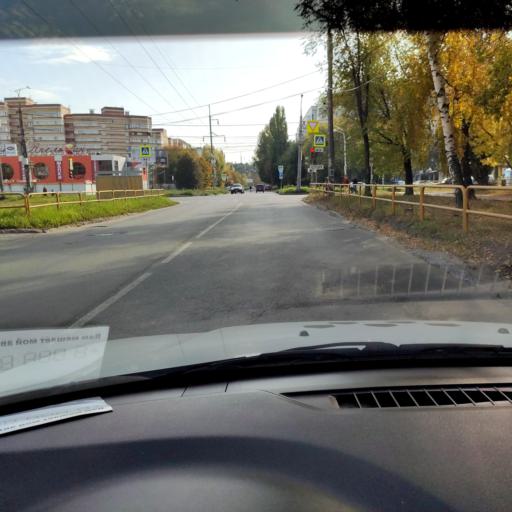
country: RU
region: Samara
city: Tol'yatti
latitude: 53.5118
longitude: 49.4424
